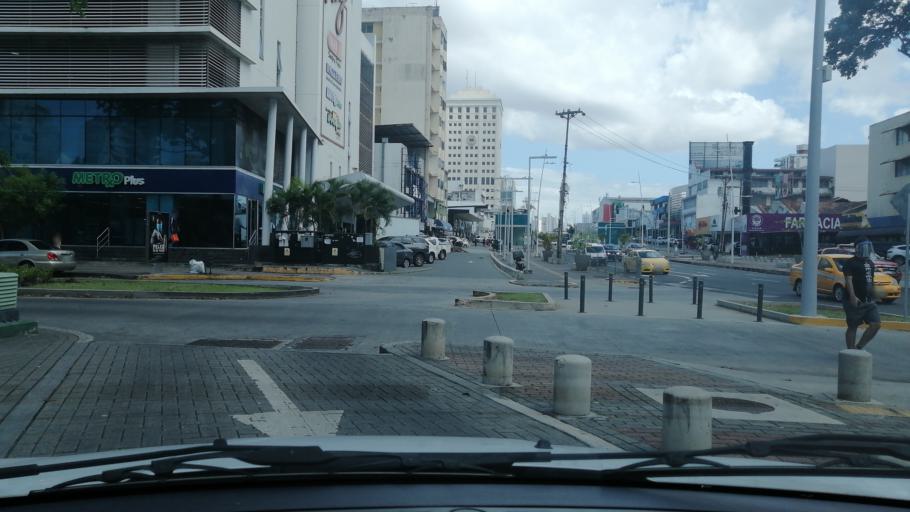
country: PA
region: Panama
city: Panama
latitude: 8.9877
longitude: -79.5234
